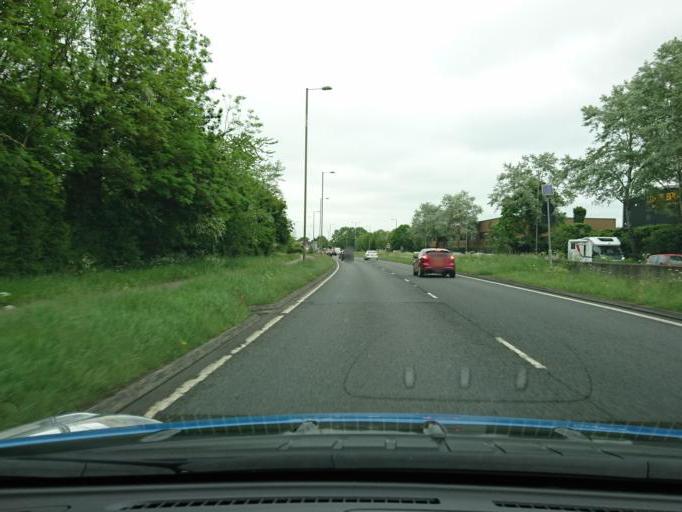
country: GB
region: England
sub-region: Oxfordshire
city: Cowley
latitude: 51.7572
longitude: -1.1947
